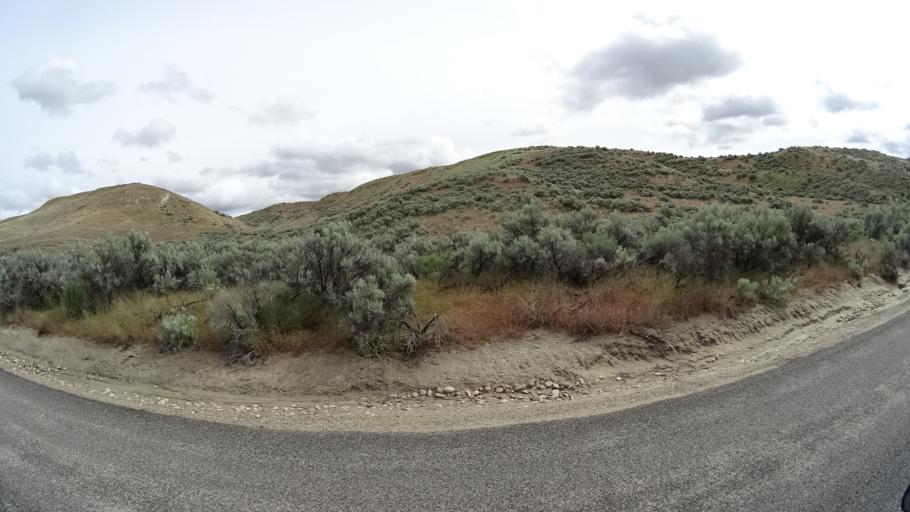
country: US
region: Idaho
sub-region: Ada County
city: Eagle
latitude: 43.7546
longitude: -116.3643
